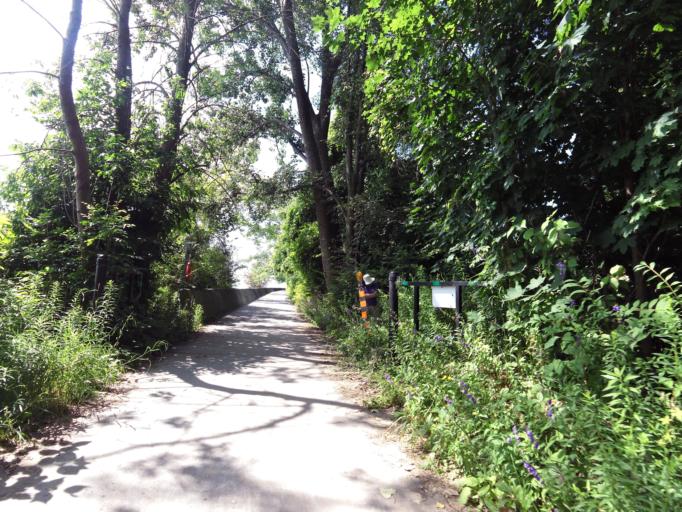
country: CA
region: Ontario
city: Toronto
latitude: 43.6293
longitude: -79.3548
